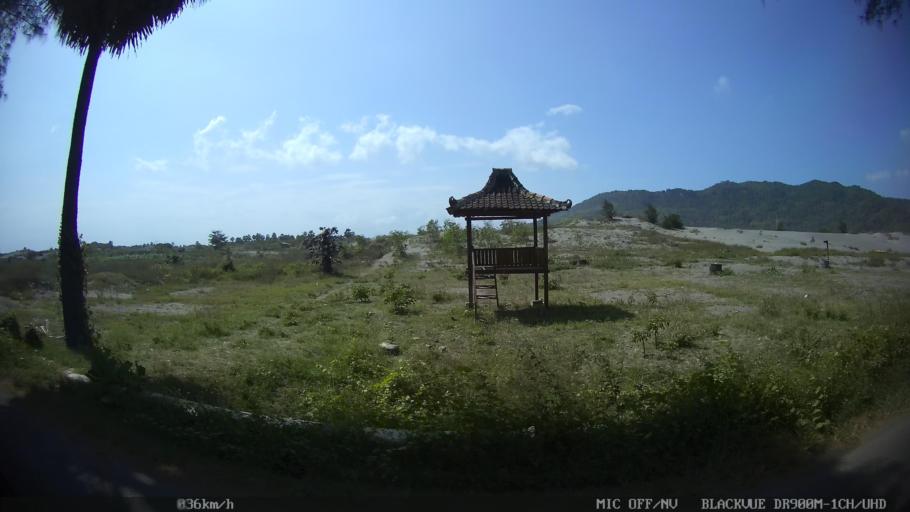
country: ID
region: Daerah Istimewa Yogyakarta
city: Pundong
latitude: -8.0179
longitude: 110.3144
